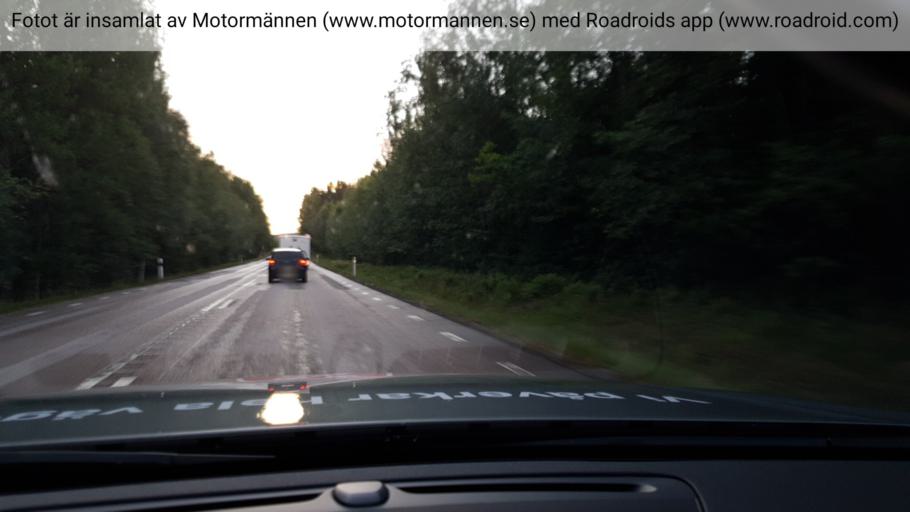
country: SE
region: Vaestmanland
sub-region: Skinnskattebergs Kommun
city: Skinnskatteberg
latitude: 59.9105
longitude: 15.7177
